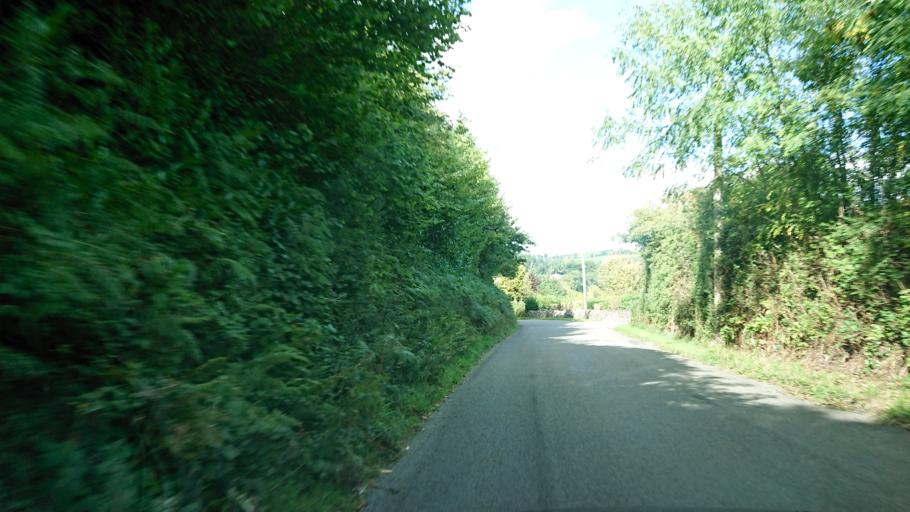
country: IE
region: Munster
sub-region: Waterford
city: Dungarvan
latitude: 52.1199
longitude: -7.6873
